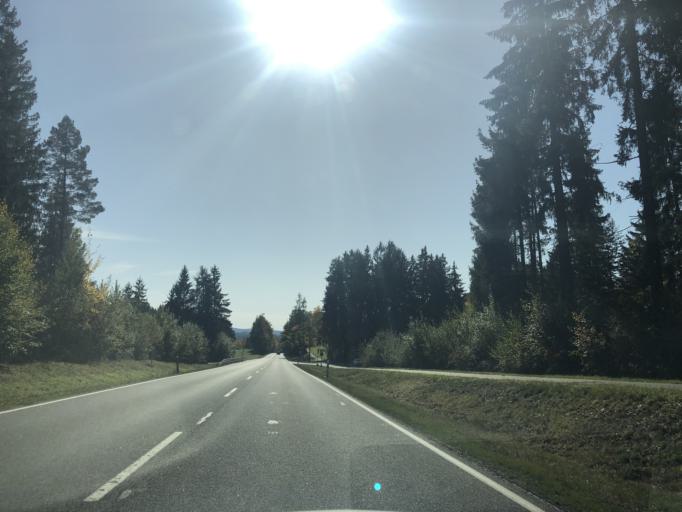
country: DE
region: Bavaria
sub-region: Lower Bavaria
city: Langdorf
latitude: 48.9955
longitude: 13.1373
